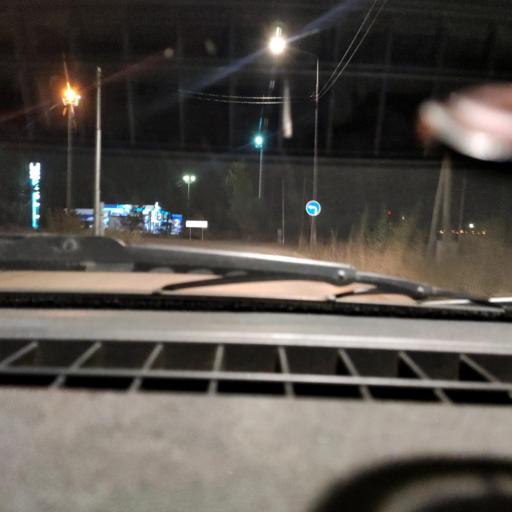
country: RU
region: Bashkortostan
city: Ufa
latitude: 54.8282
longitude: 56.1250
